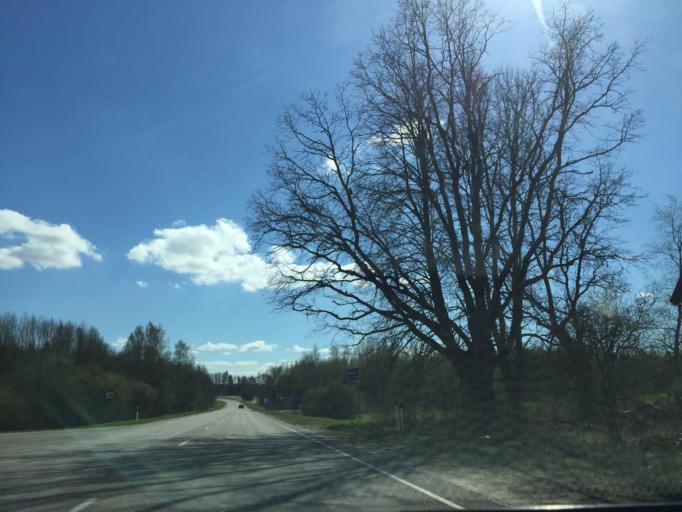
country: EE
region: Valgamaa
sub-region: Valga linn
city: Valga
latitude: 57.8706
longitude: 26.0592
